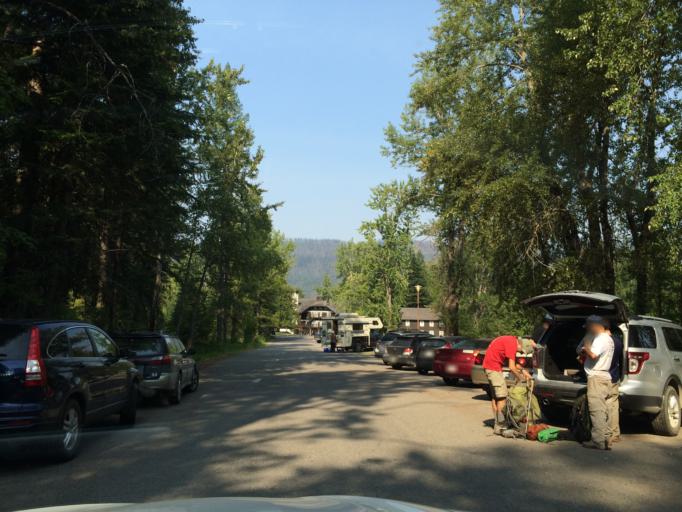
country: US
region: Montana
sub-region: Flathead County
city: Columbia Falls
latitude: 48.6171
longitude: -113.8763
